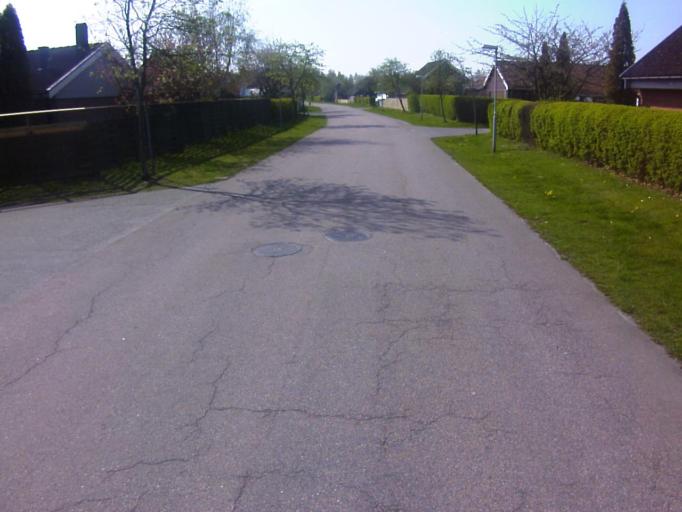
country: SE
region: Skane
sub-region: Kavlinge Kommun
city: Loddekopinge
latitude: 55.7655
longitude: 13.0007
